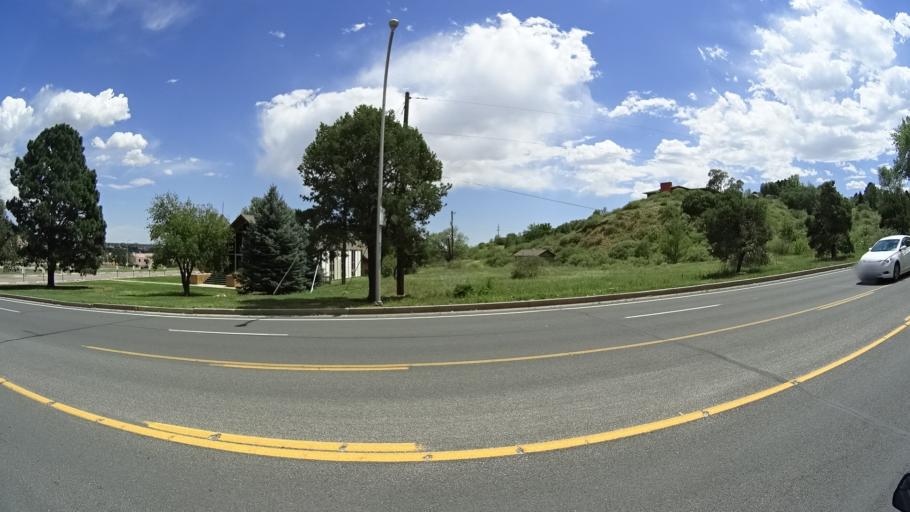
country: US
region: Colorado
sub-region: El Paso County
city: Stratmoor
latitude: 38.7862
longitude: -104.7971
